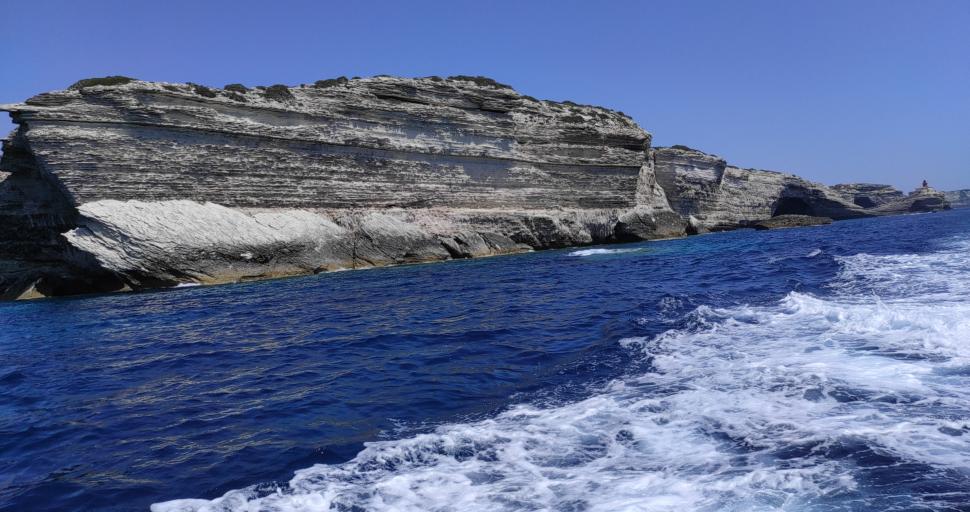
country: FR
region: Corsica
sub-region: Departement de la Corse-du-Sud
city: Bonifacio
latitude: 41.3902
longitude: 9.1368
